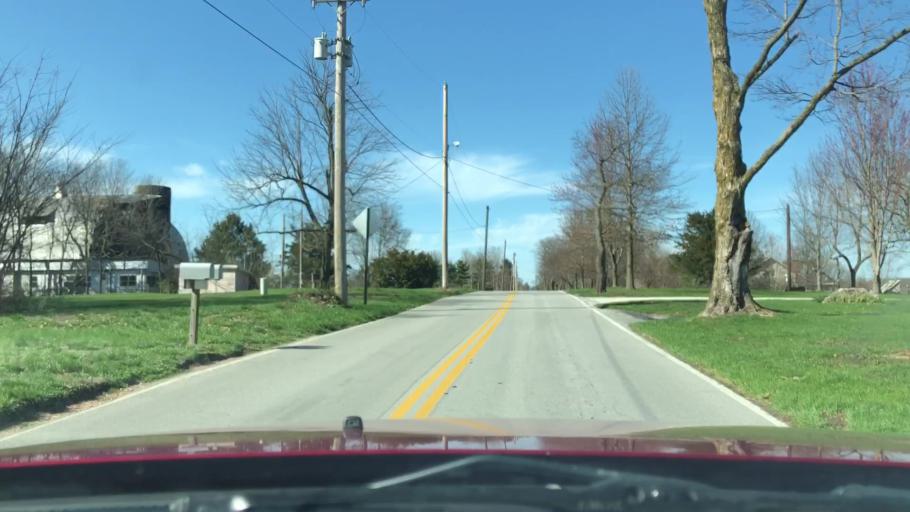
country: US
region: Missouri
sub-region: Greene County
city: Strafford
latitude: 37.2249
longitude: -93.1884
